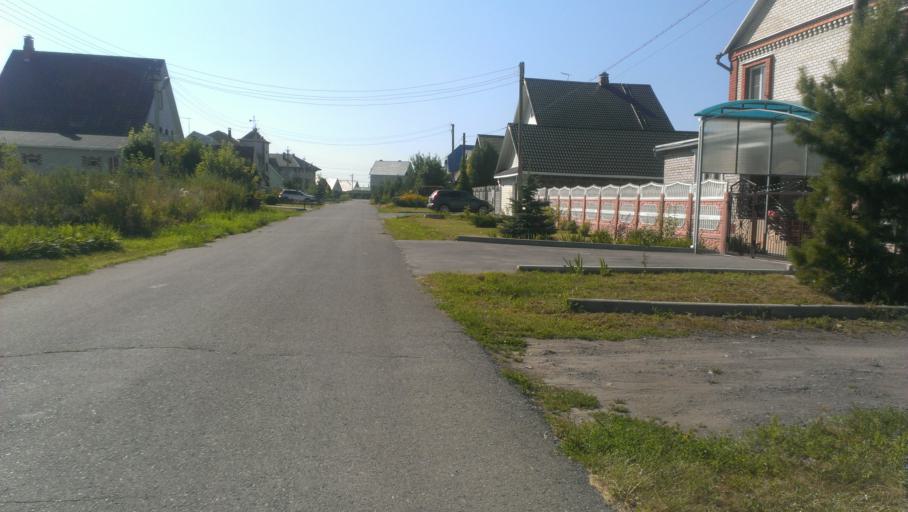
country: RU
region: Altai Krai
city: Novosilikatnyy
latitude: 53.3703
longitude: 83.6550
